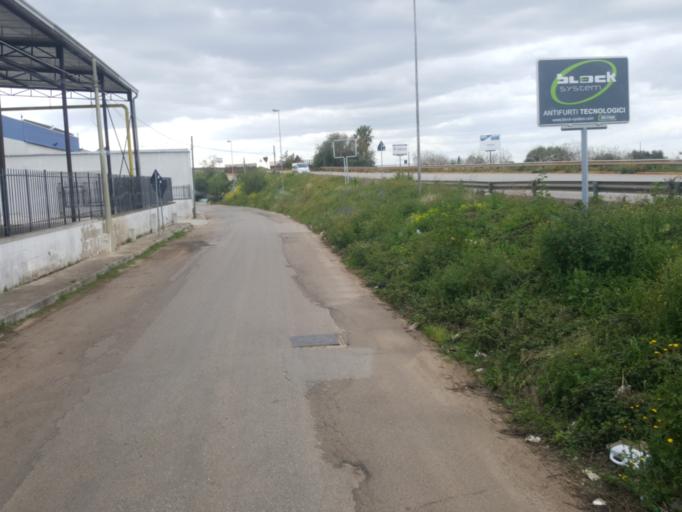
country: IT
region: Apulia
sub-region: Provincia di Bari
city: Conversano
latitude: 40.9780
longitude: 17.1108
